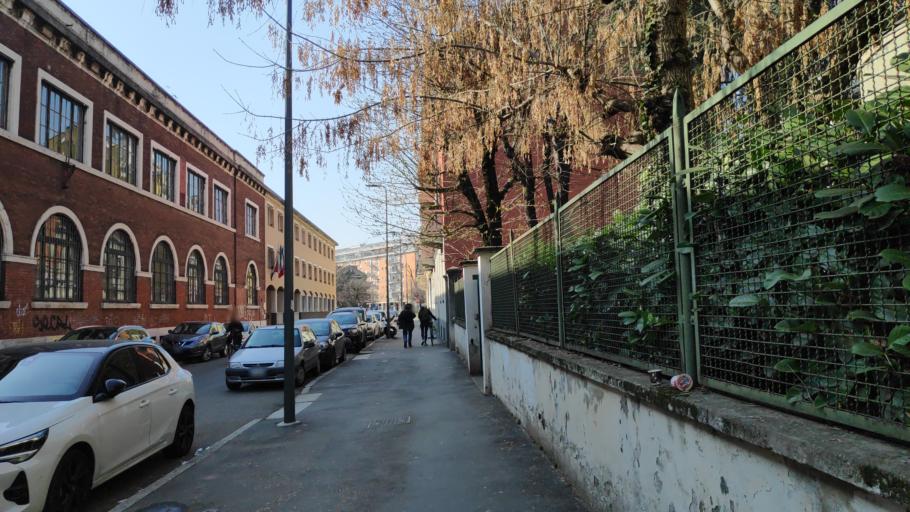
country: IT
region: Lombardy
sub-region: Citta metropolitana di Milano
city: Sesto San Giovanni
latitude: 45.5037
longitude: 9.2446
